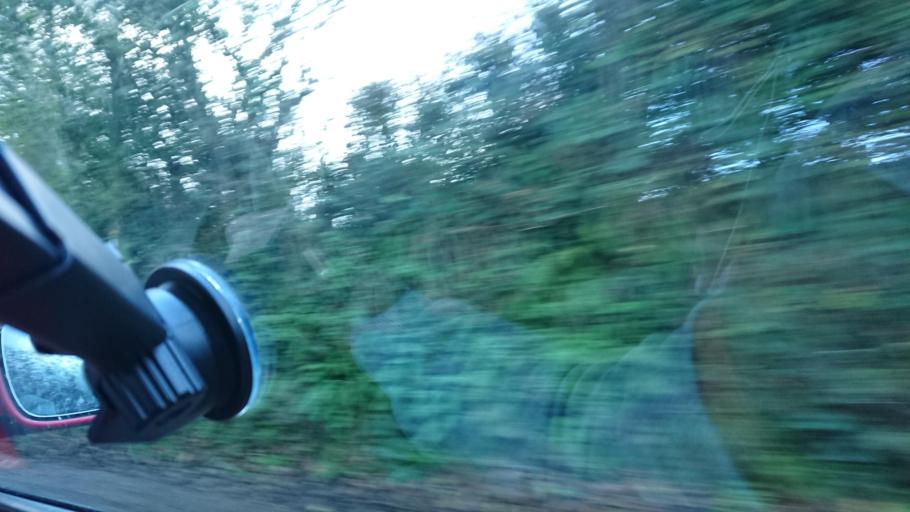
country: GB
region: England
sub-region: Cornwall
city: Looe
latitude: 50.3461
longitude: -4.4757
